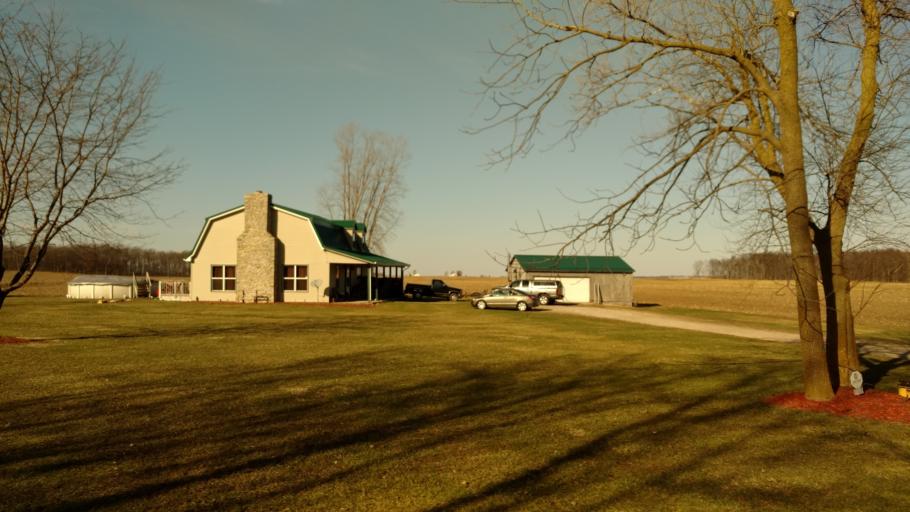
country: US
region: Ohio
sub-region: Crawford County
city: Bucyrus
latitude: 40.7034
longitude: -82.9901
